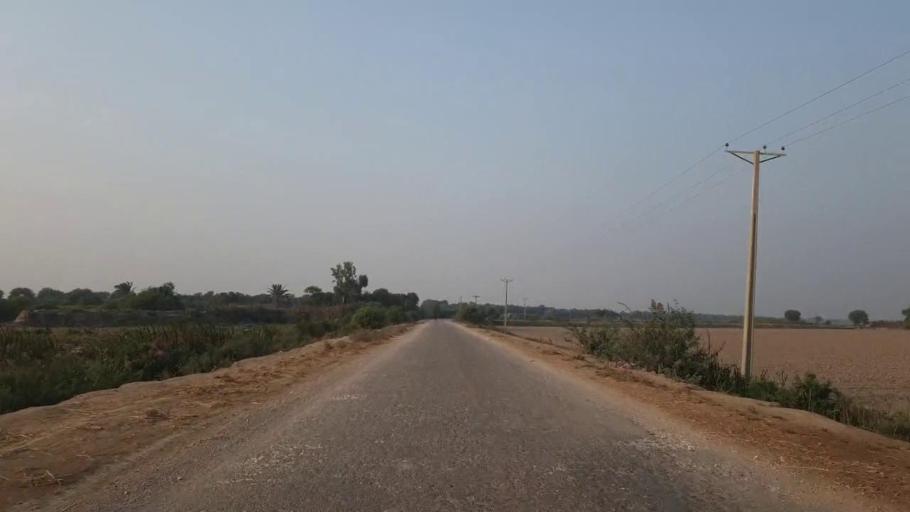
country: PK
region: Sindh
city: Tando Muhammad Khan
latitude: 25.1126
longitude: 68.4284
